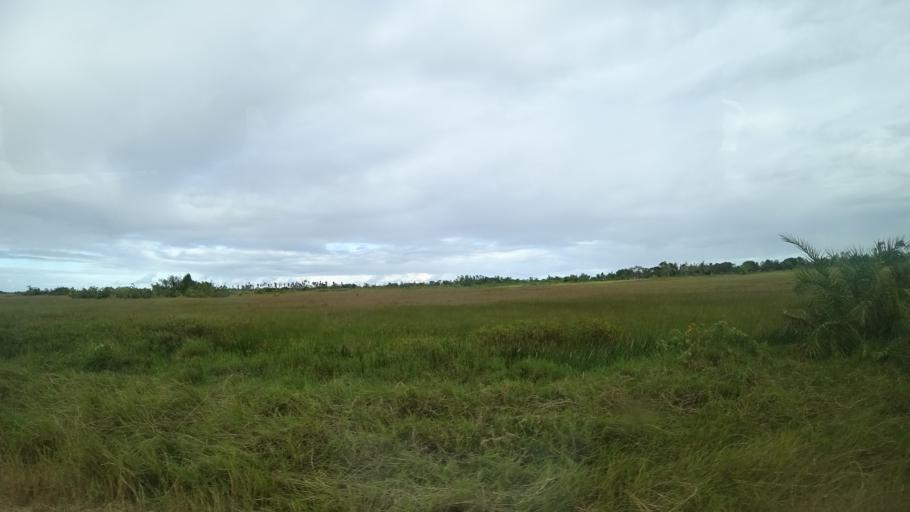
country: MZ
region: Sofala
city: Beira
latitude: -19.7115
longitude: 35.0153
